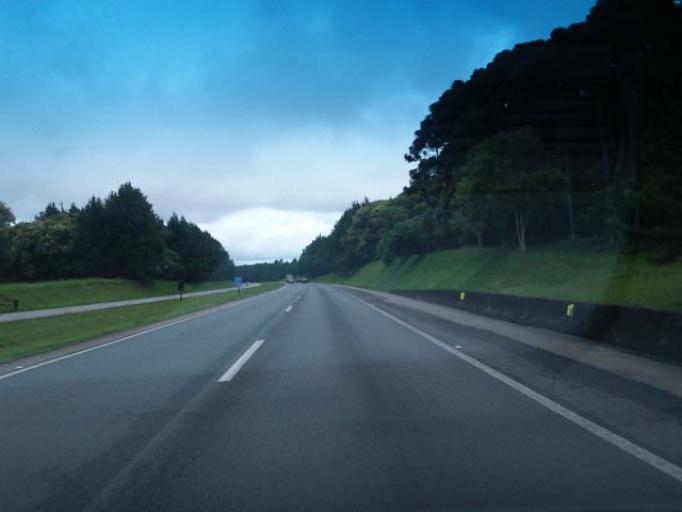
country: BR
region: Parana
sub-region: Piraquara
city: Piraquara
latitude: -25.4101
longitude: -49.0634
